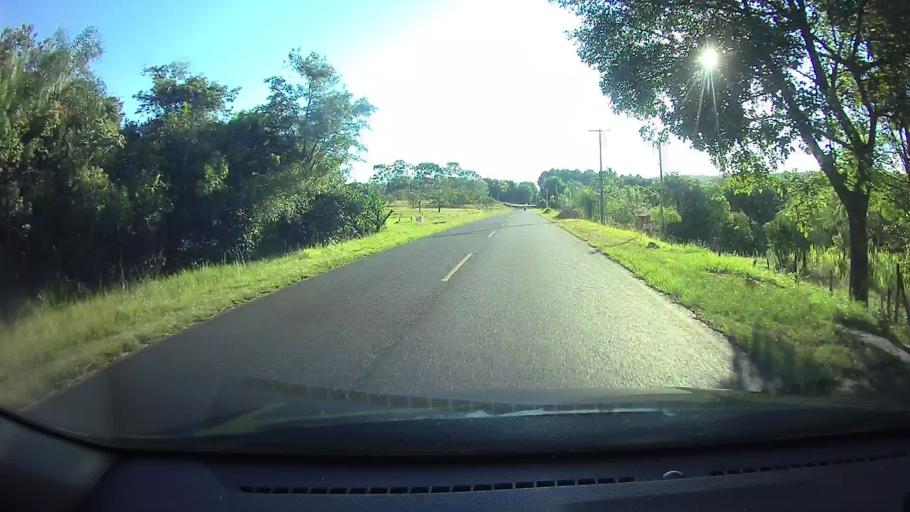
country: PY
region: Cordillera
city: Emboscada
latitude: -25.1722
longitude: -57.2812
